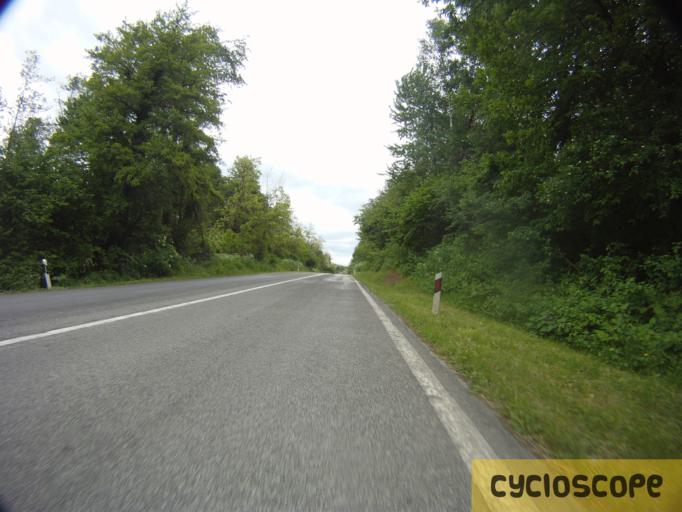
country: SI
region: Crnomelj
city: Crnomelj
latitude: 45.4472
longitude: 15.3220
